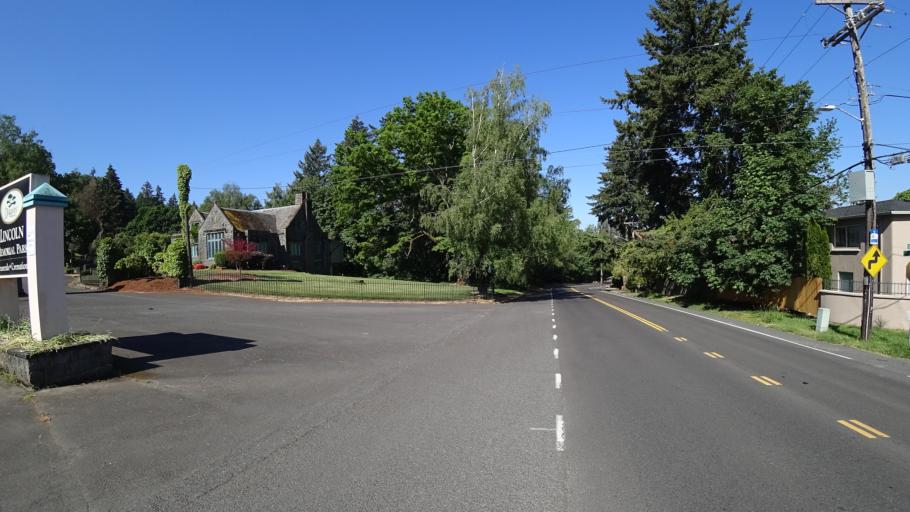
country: US
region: Oregon
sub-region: Multnomah County
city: Lents
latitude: 45.4646
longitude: -122.5557
